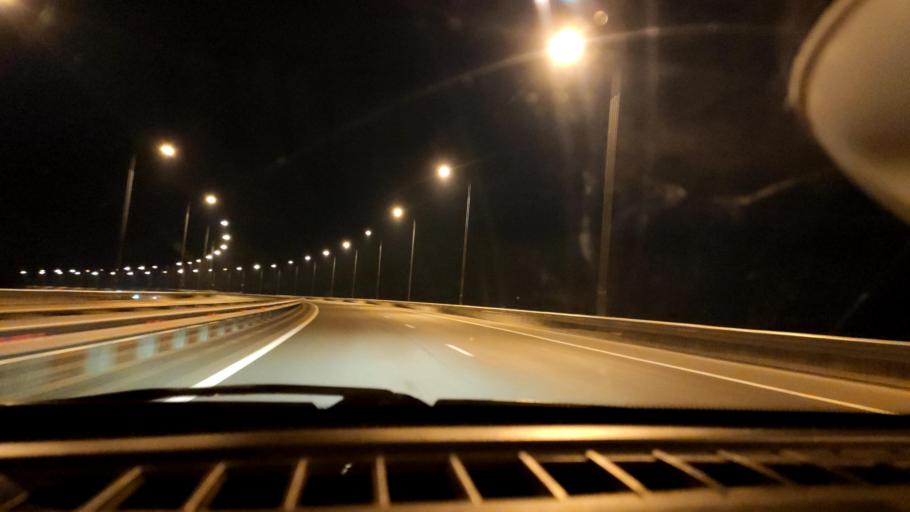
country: RU
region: Samara
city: Bereza
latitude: 53.5035
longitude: 50.1185
